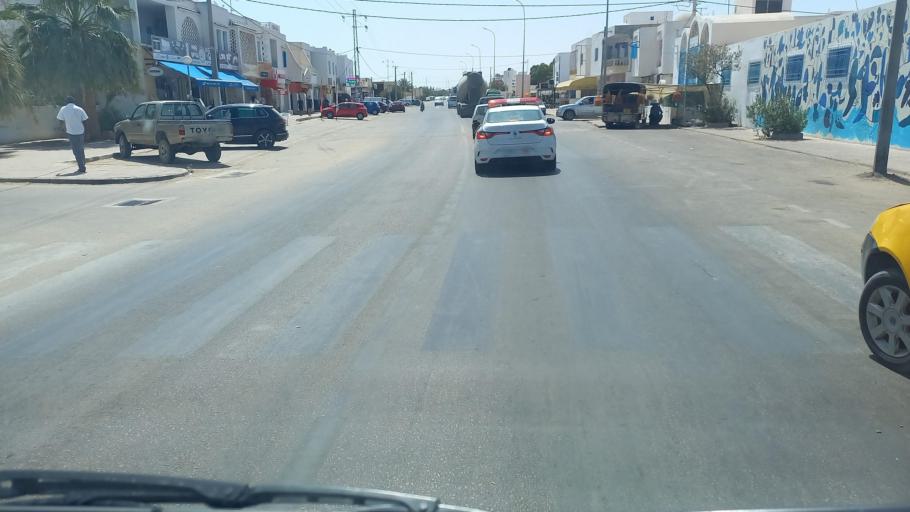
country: TN
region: Madanin
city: Houmt Souk
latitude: 33.8002
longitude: 10.8835
